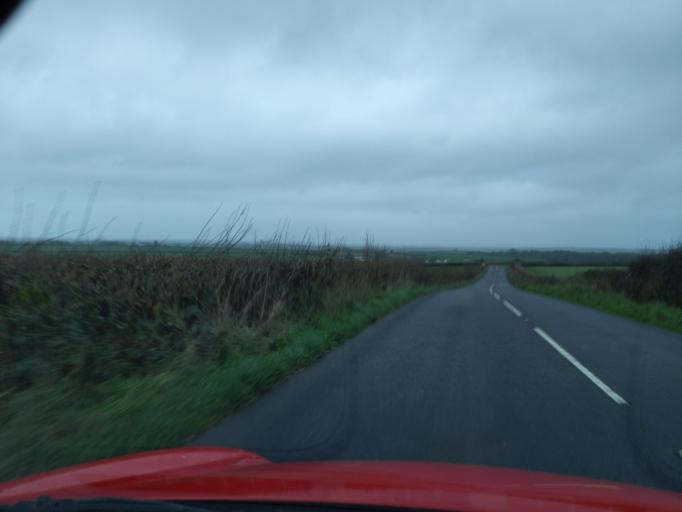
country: GB
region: England
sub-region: Devon
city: Holsworthy
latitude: 50.7503
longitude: -4.3272
